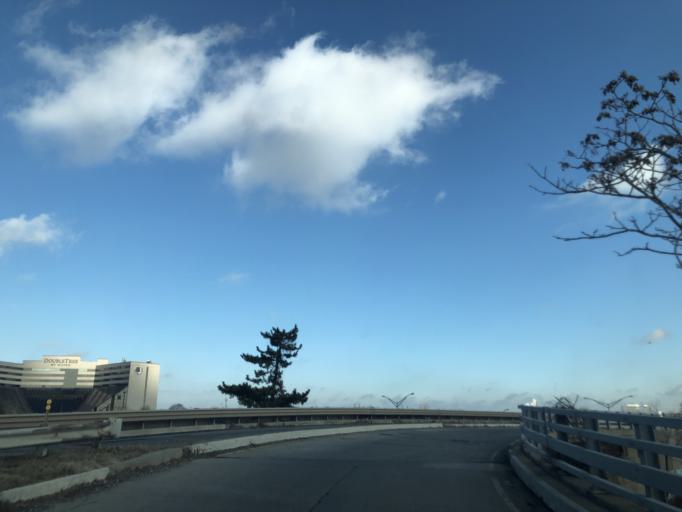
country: US
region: New Jersey
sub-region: Essex County
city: Newark
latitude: 40.7096
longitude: -74.1645
